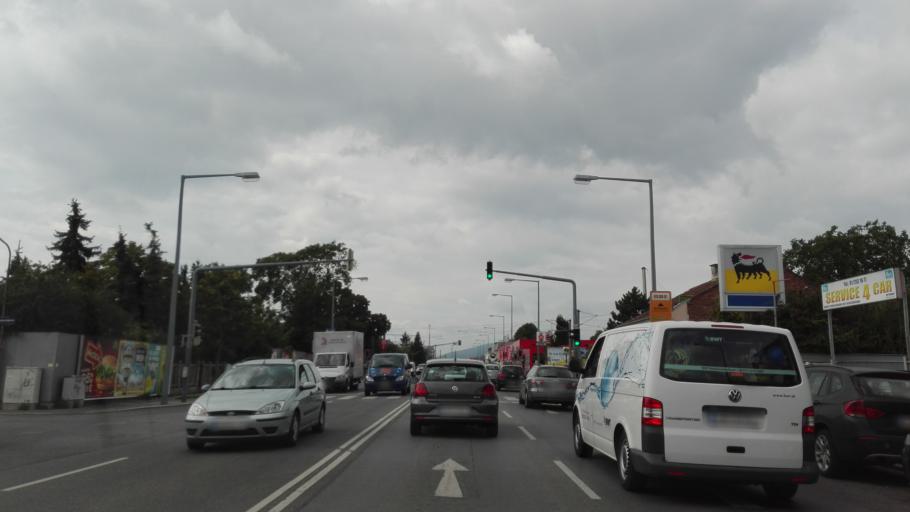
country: AT
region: Lower Austria
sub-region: Politischer Bezirk Modling
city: Vosendorf
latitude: 48.1410
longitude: 16.3288
